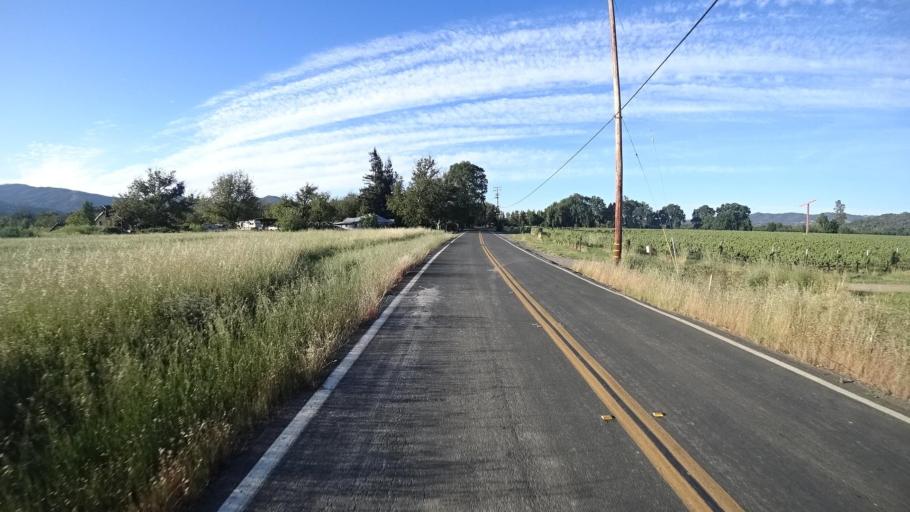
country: US
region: California
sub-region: Lake County
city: Upper Lake
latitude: 39.1885
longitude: -122.9010
